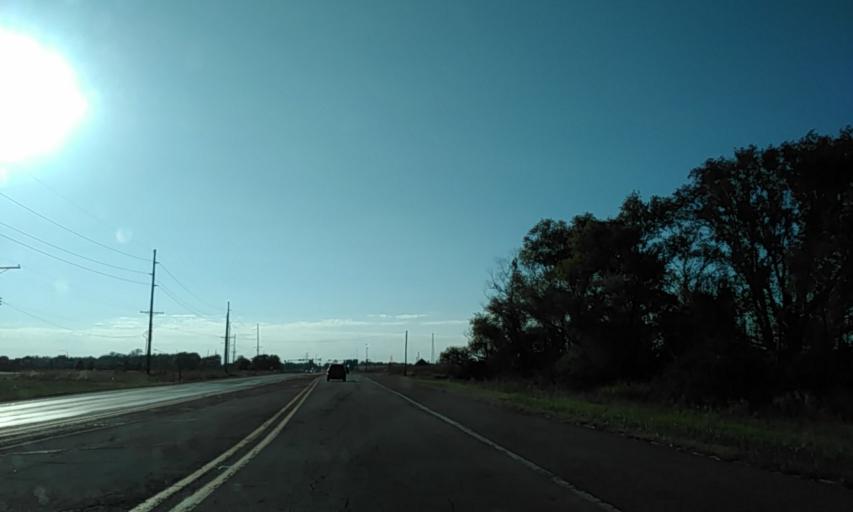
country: US
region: Illinois
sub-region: Madison County
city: Troy
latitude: 38.7175
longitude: -89.9057
